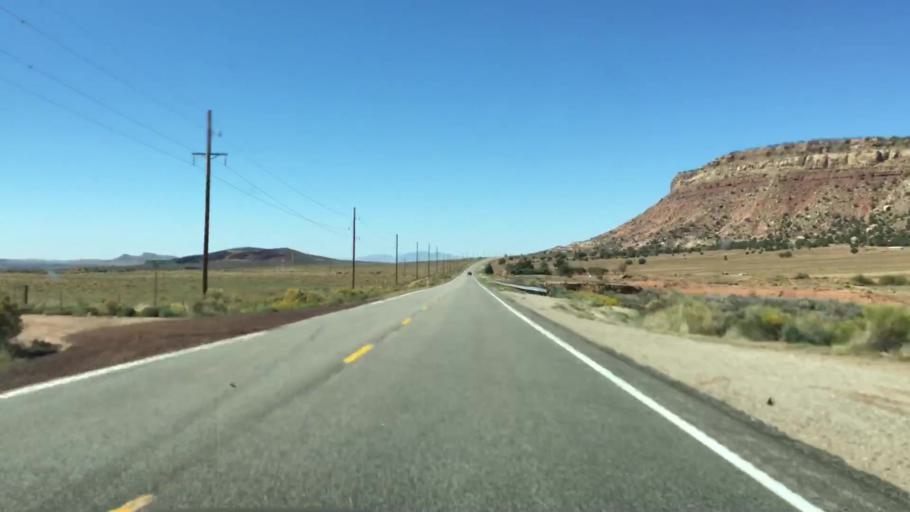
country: US
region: Utah
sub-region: Washington County
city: LaVerkin
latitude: 37.1178
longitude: -113.1640
